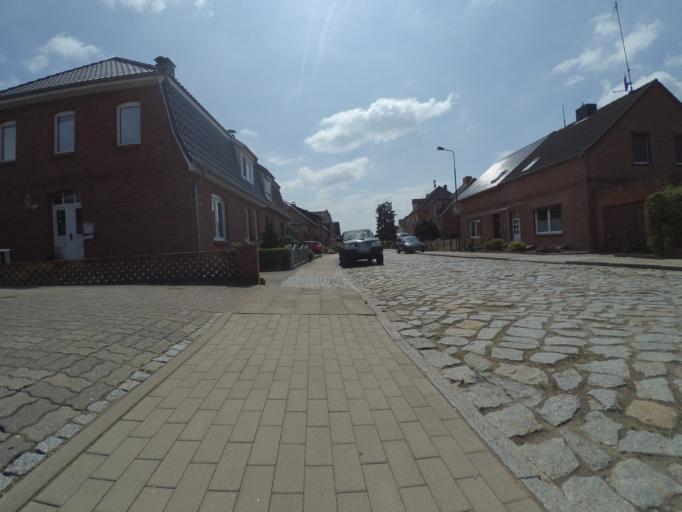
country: DE
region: Mecklenburg-Vorpommern
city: Lubz
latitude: 53.4592
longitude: 12.0411
